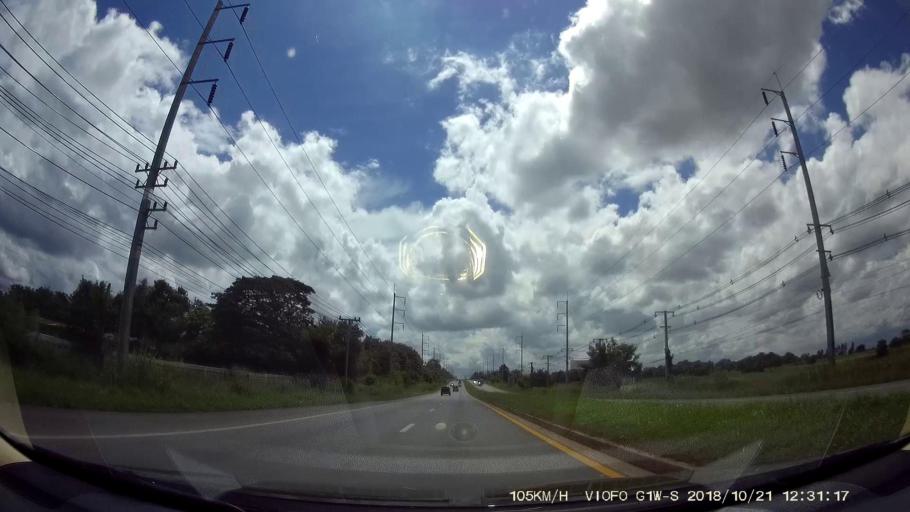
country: TH
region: Nakhon Ratchasima
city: Dan Khun Thot
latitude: 15.1588
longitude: 101.7356
